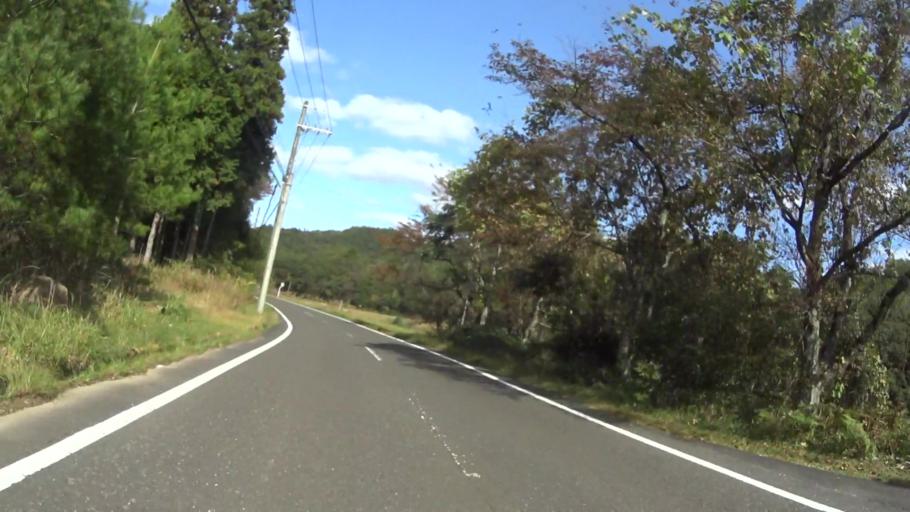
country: JP
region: Hyogo
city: Toyooka
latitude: 35.5555
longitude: 134.9780
